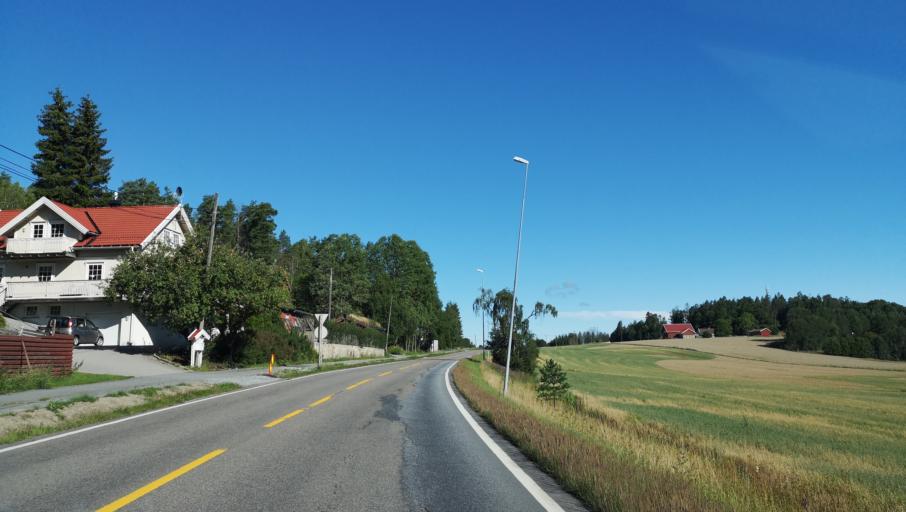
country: NO
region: Ostfold
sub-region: Spydeberg
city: Spydeberg
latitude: 59.5900
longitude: 11.1120
